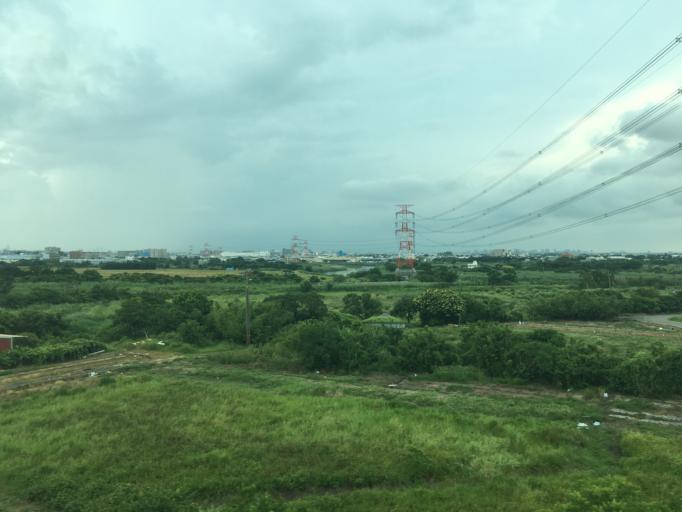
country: TW
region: Taiwan
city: Taoyuan City
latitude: 25.0826
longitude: 121.2747
